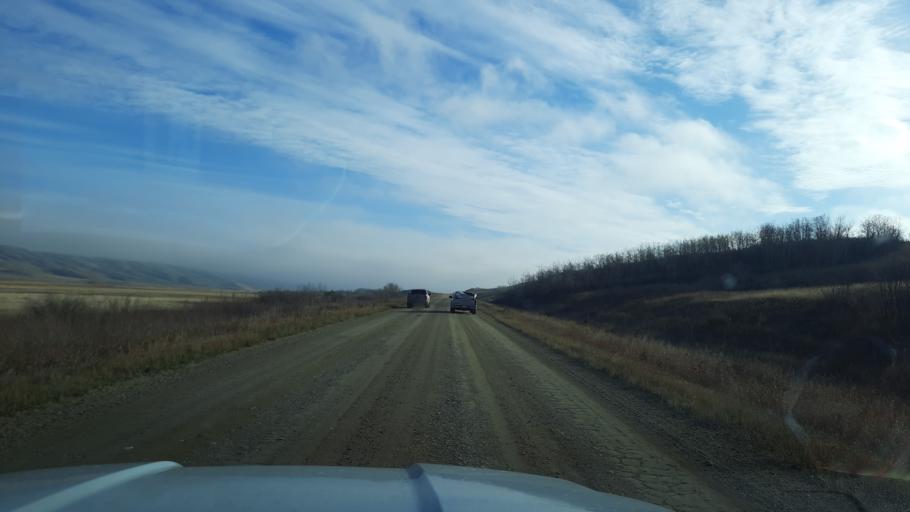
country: CA
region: Saskatchewan
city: Pilot Butte
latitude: 50.7839
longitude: -104.2356
